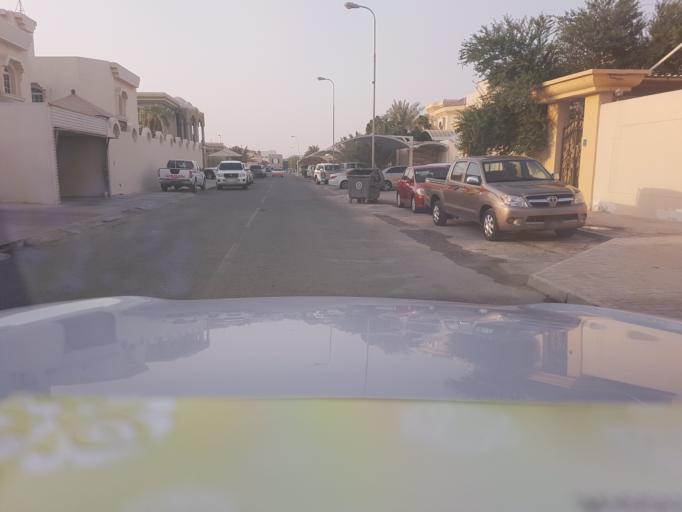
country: QA
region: Baladiyat ad Dawhah
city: Doha
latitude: 25.2348
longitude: 51.5644
